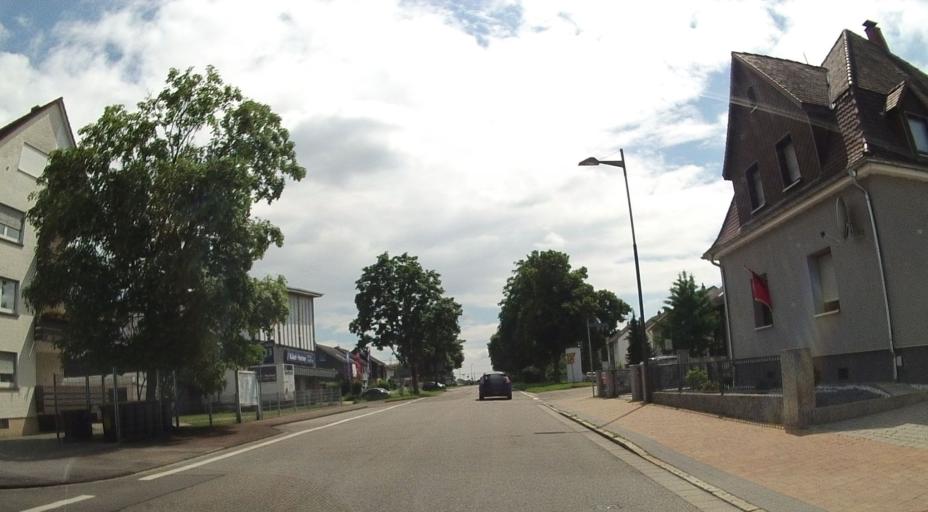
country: DE
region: Baden-Wuerttemberg
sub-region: Karlsruhe Region
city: Durmersheim
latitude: 48.9251
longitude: 8.2645
